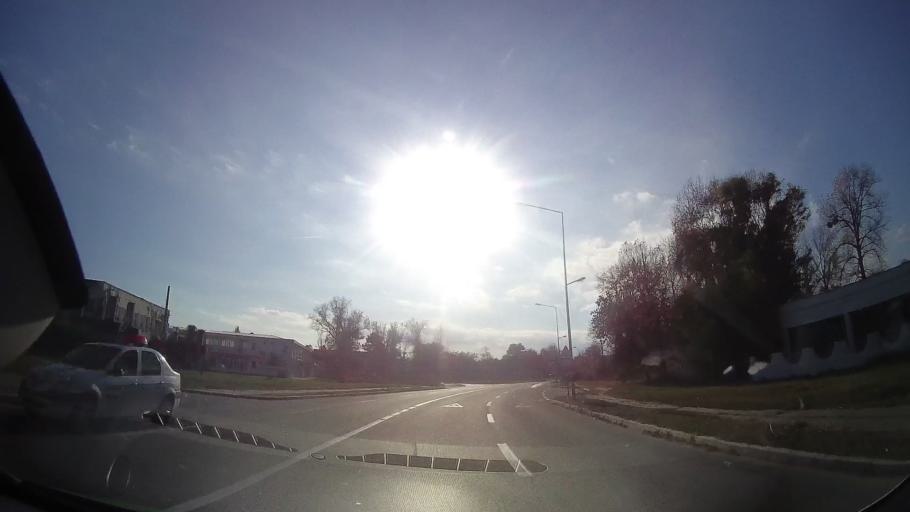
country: RO
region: Constanta
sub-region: Municipiul Mangalia
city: Mangalia
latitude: 43.8318
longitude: 28.5877
